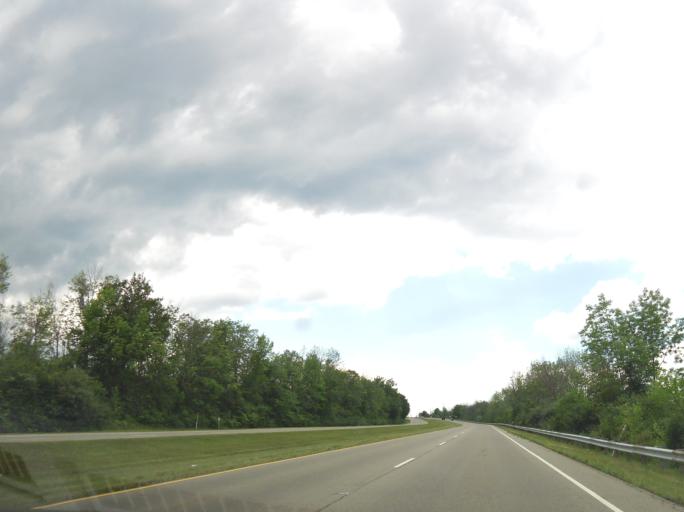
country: US
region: Ohio
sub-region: Greene County
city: Wright-Patterson AFB
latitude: 39.7957
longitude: -84.0782
